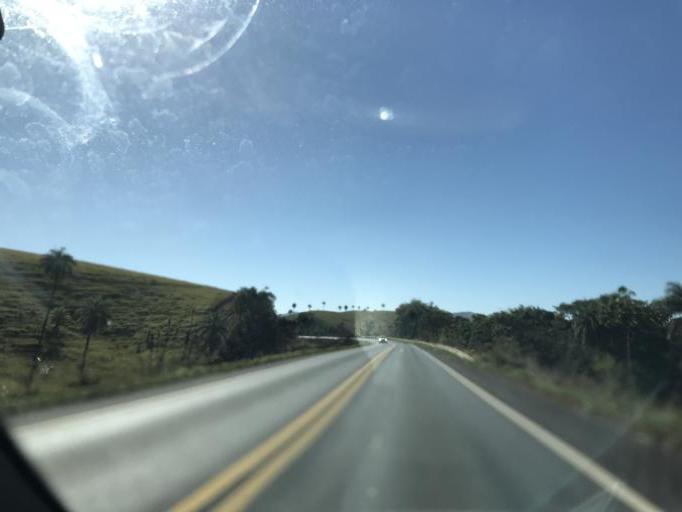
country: BR
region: Minas Gerais
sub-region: Bambui
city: Bambui
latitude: -19.8354
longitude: -46.0028
